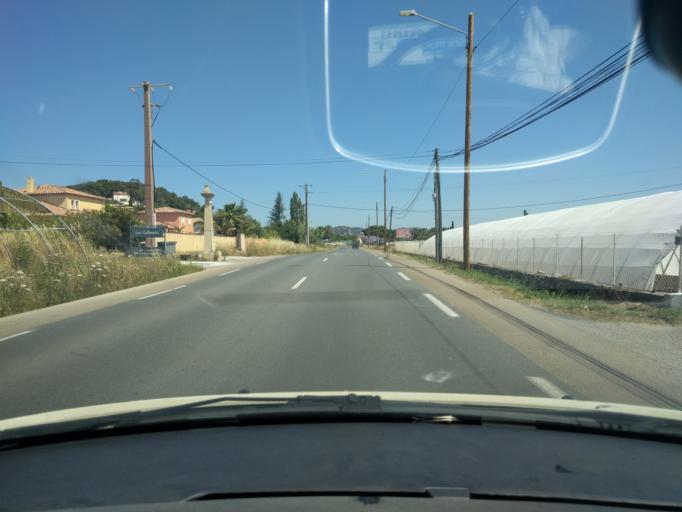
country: FR
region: Provence-Alpes-Cote d'Azur
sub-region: Departement du Var
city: Hyeres
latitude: 43.0902
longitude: 6.1292
